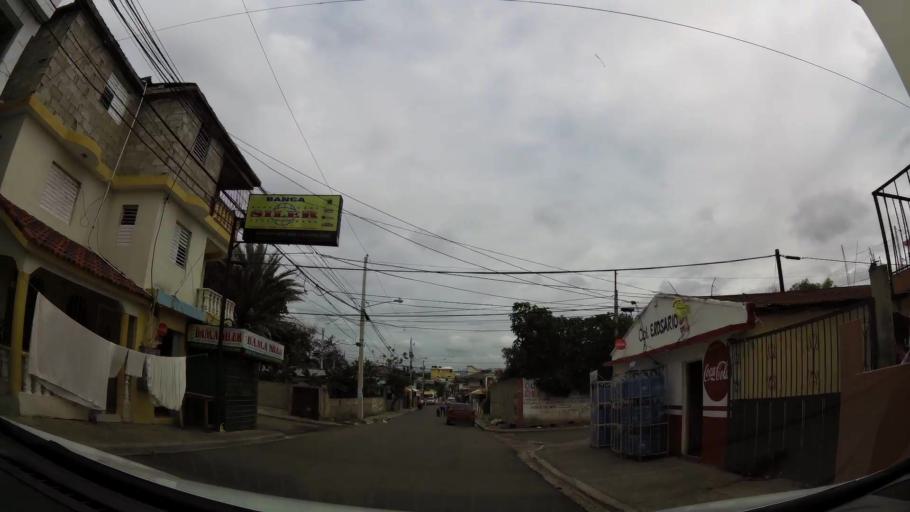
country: DO
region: Santiago
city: Santiago de los Caballeros
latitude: 19.4283
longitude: -70.6677
